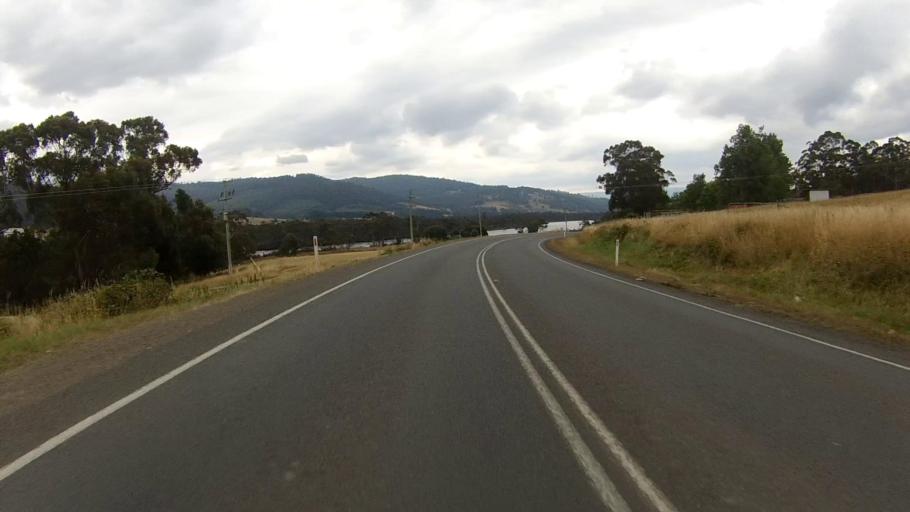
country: AU
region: Tasmania
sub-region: Huon Valley
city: Franklin
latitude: -43.0869
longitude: 147.0296
